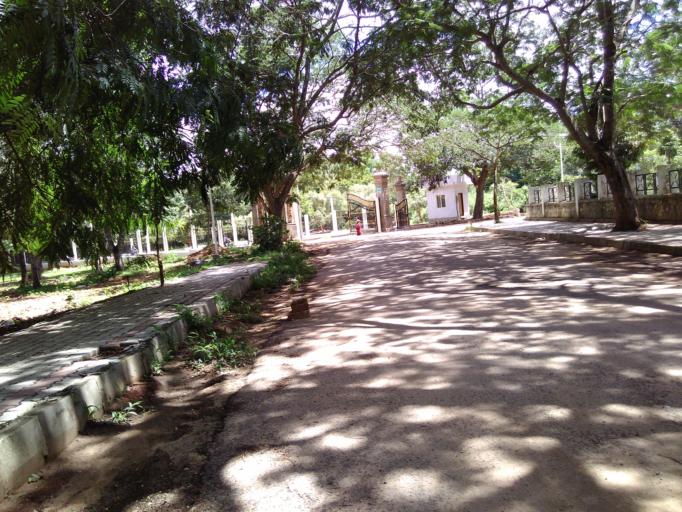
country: IN
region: Karnataka
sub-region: Mysore
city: Mysore
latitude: 12.3141
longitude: 76.6260
